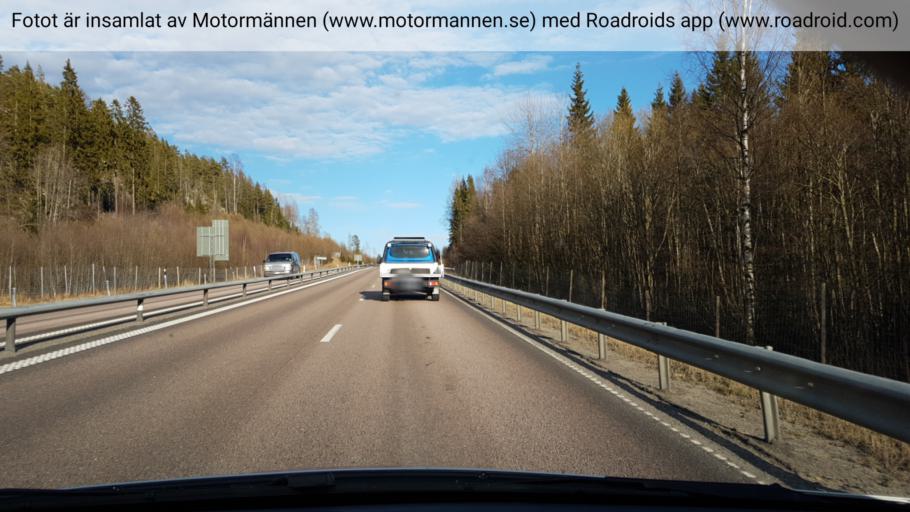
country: SE
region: Vaesternorrland
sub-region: OErnskoeldsviks Kommun
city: Ornskoldsvik
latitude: 63.3156
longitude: 18.8070
